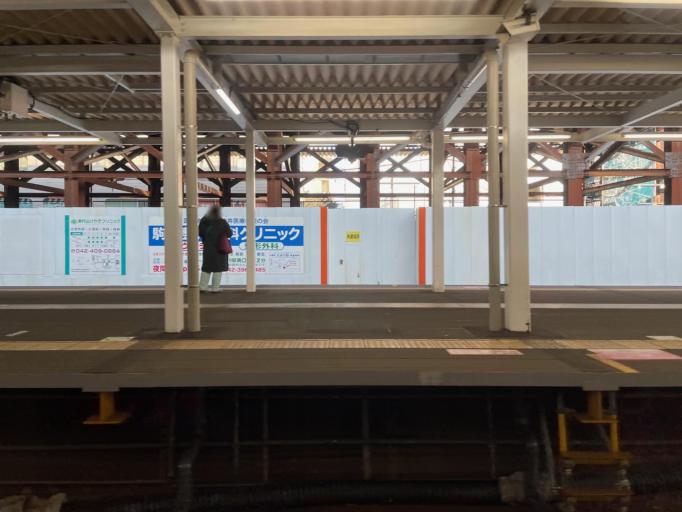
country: JP
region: Tokyo
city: Higashimurayama-shi
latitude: 35.7597
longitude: 139.4659
